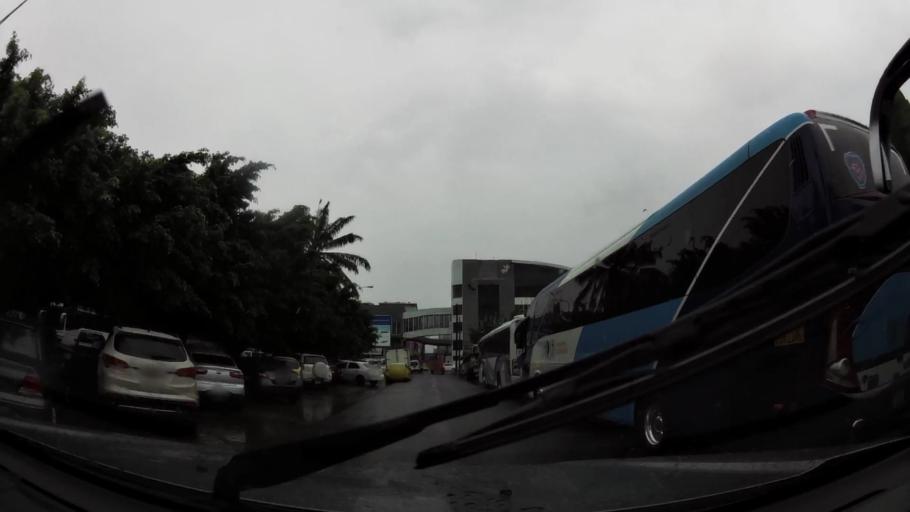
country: PA
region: Colon
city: Colon
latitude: 9.3562
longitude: -79.8951
